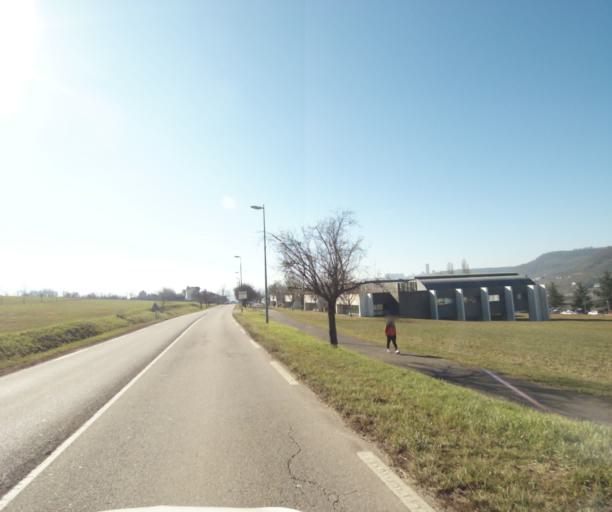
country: FR
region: Lorraine
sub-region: Departement de Meurthe-et-Moselle
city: Malzeville
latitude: 48.7285
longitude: 6.1823
